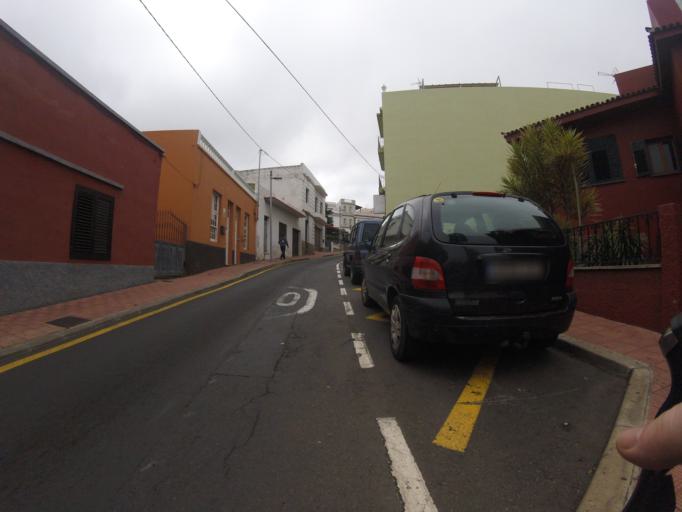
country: ES
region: Canary Islands
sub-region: Provincia de Santa Cruz de Tenerife
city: Tegueste
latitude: 28.5332
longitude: -16.3597
